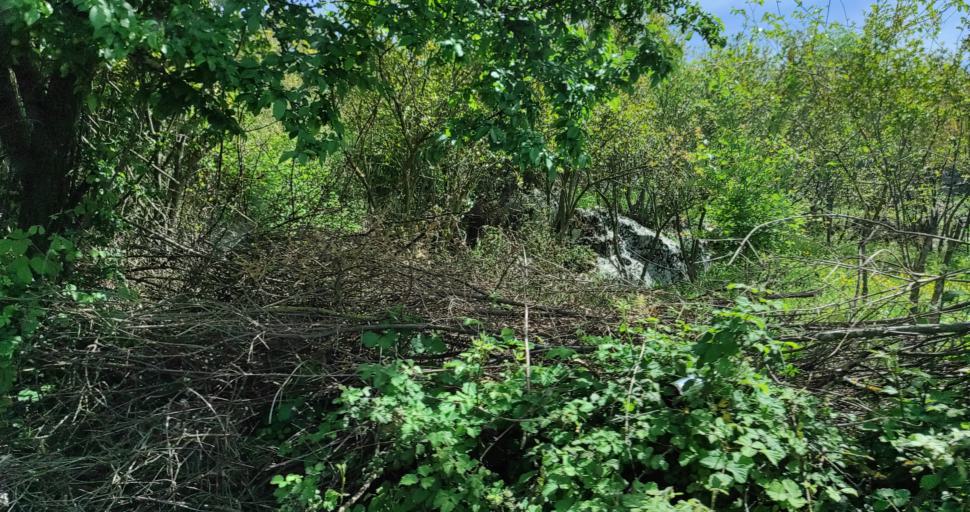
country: AL
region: Shkoder
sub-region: Rrethi i Malesia e Madhe
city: Gruemire
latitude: 42.1423
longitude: 19.5478
